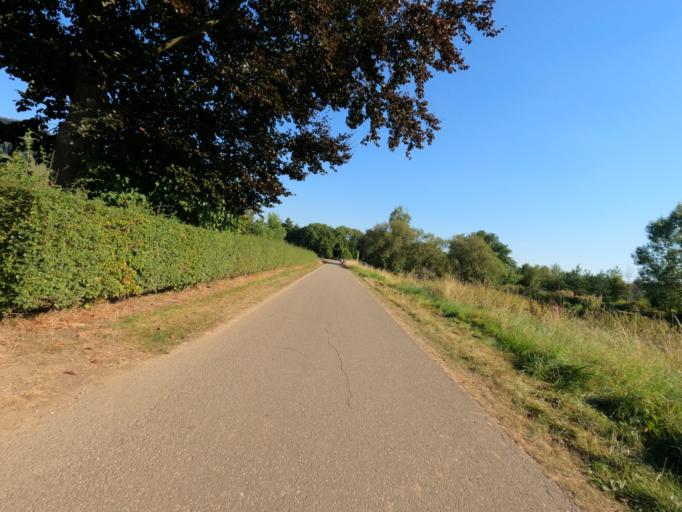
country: NL
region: Limburg
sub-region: Gemeente Roerdalen
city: Vlodrop
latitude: 51.1327
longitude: 6.0887
